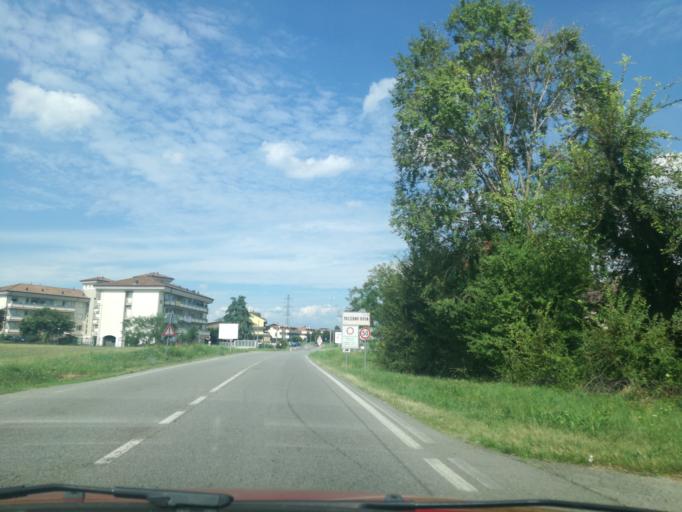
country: IT
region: Lombardy
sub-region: Citta metropolitana di Milano
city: Trezzano Rosa
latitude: 45.5816
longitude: 9.4799
